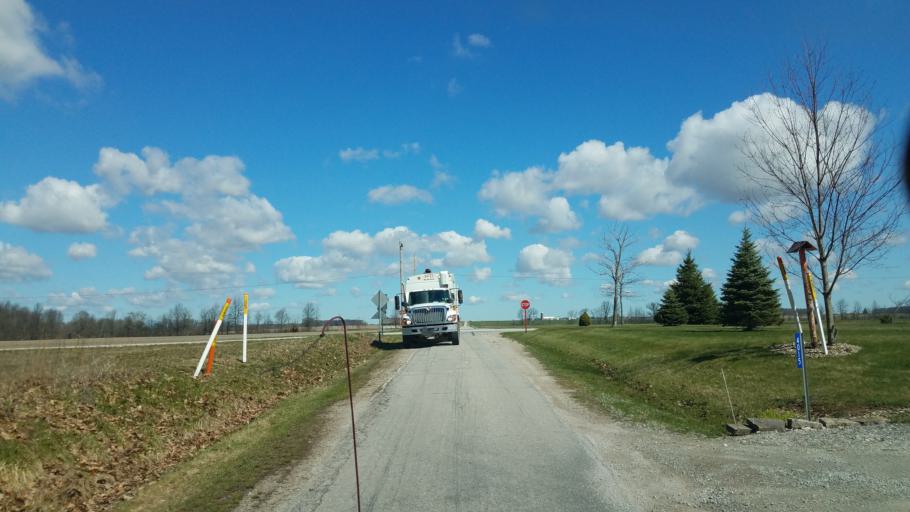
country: US
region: Ohio
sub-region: Sandusky County
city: Mount Carmel
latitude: 41.0658
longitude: -82.9390
